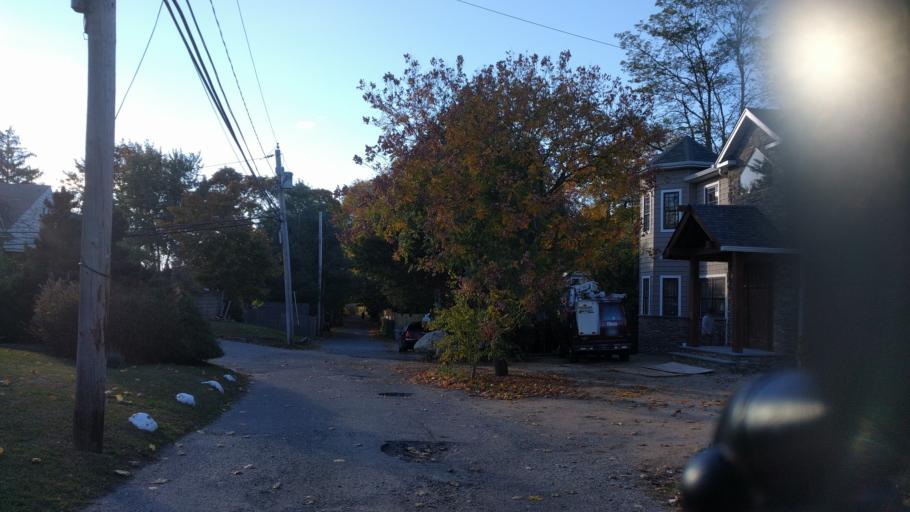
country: US
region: New York
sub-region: Nassau County
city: Bayville
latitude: 40.9086
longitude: -73.5750
